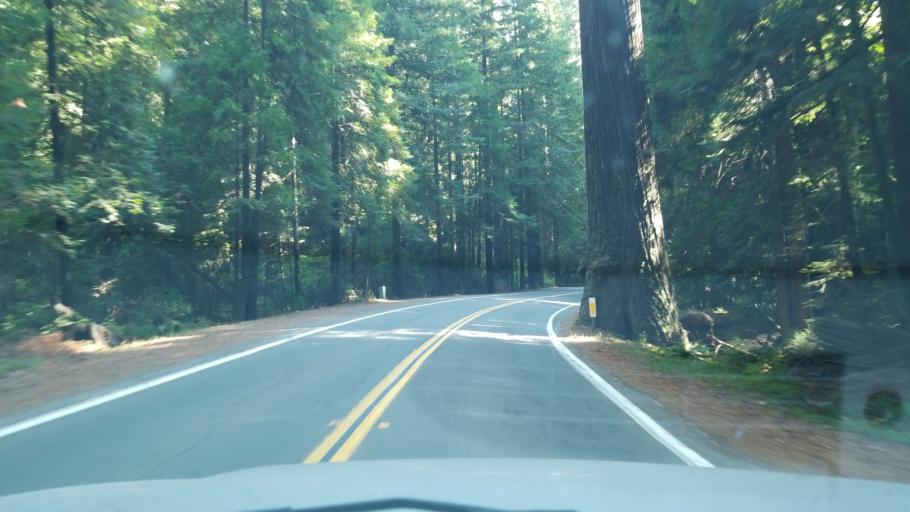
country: US
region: California
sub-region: Humboldt County
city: Redway
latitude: 40.2432
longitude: -123.8211
